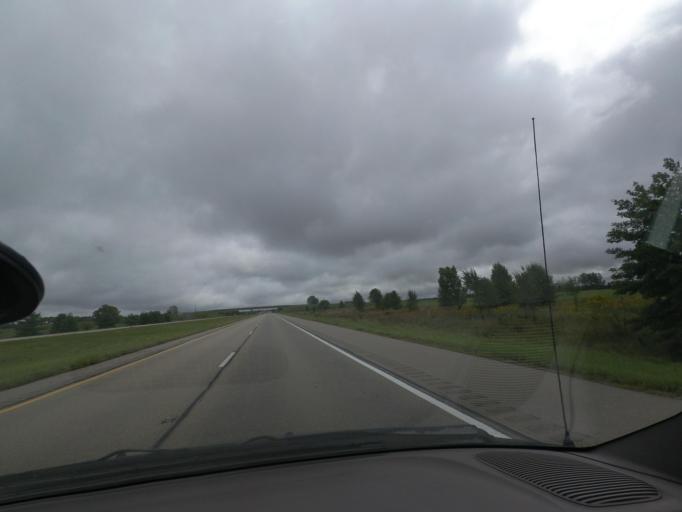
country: US
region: Illinois
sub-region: Piatt County
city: Monticello
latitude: 40.0307
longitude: -88.6356
